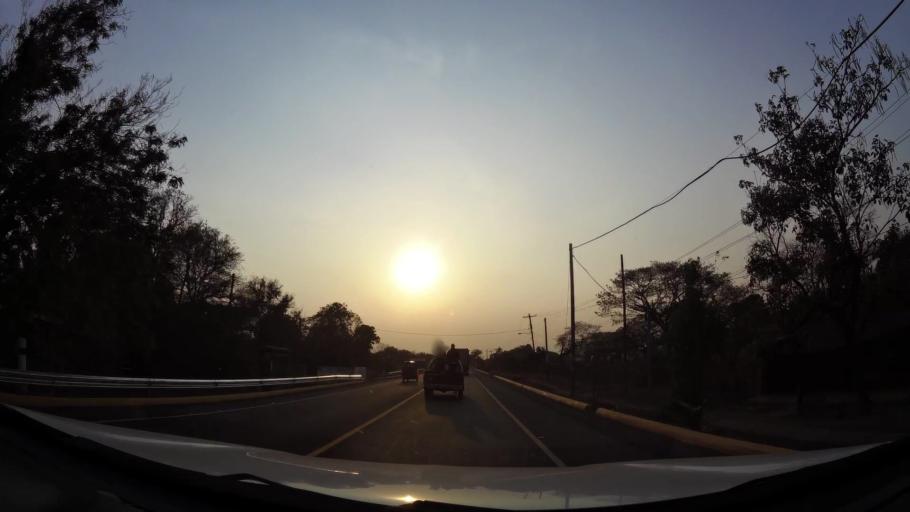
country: NI
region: Leon
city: Nagarote
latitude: 12.2724
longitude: -86.5641
